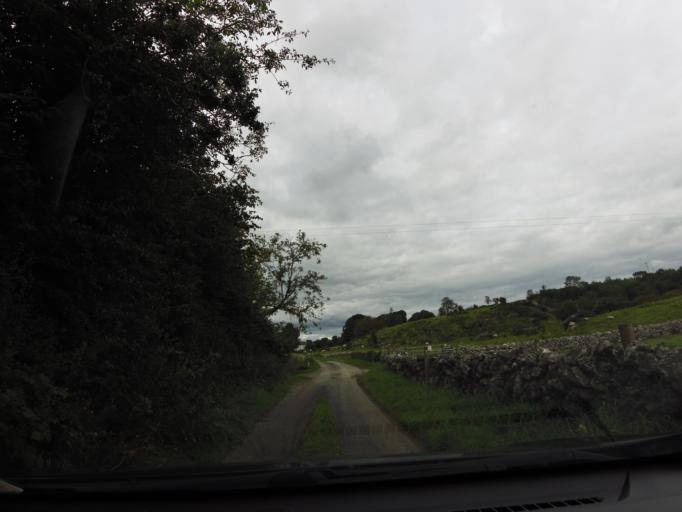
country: IE
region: Connaught
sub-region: County Galway
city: Loughrea
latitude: 53.1624
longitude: -8.4538
